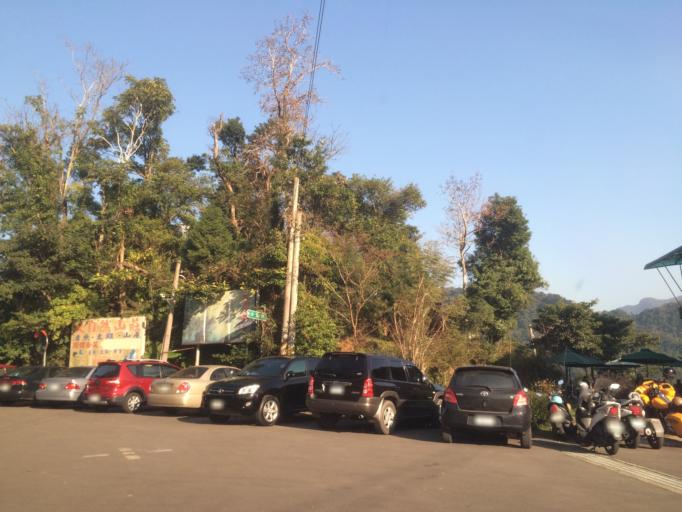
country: TW
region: Taiwan
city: Daxi
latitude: 24.8095
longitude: 121.2611
